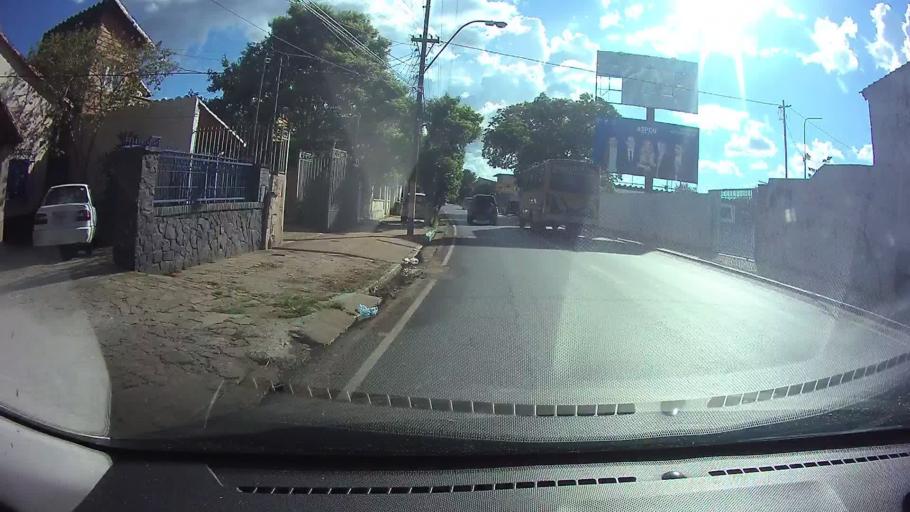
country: PY
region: Cordillera
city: Caacupe
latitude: -25.3826
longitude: -57.1373
